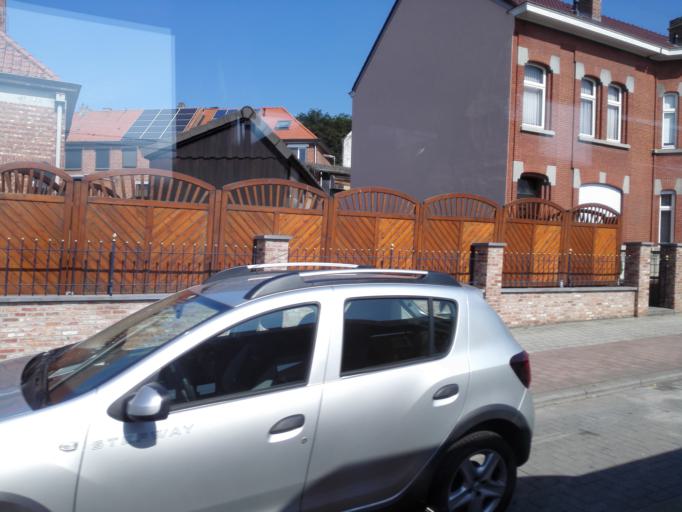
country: BE
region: Flanders
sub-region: Provincie Vlaams-Brabant
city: Diest
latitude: 50.9796
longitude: 5.0468
